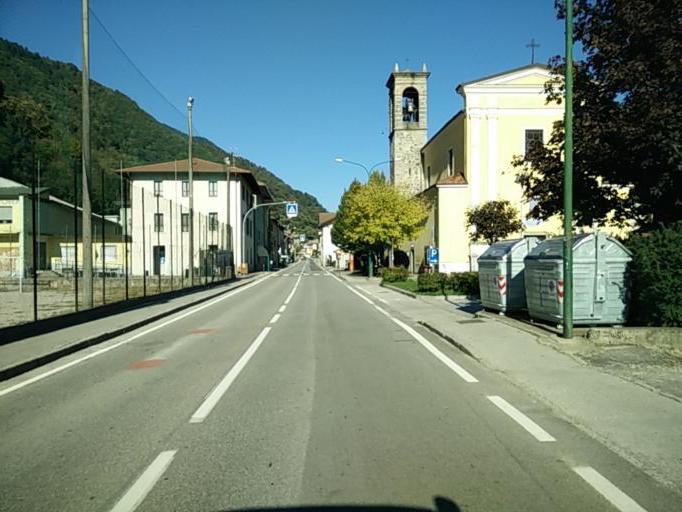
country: IT
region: Lombardy
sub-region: Provincia di Brescia
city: Ponte Caffaro
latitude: 45.8219
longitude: 10.5279
